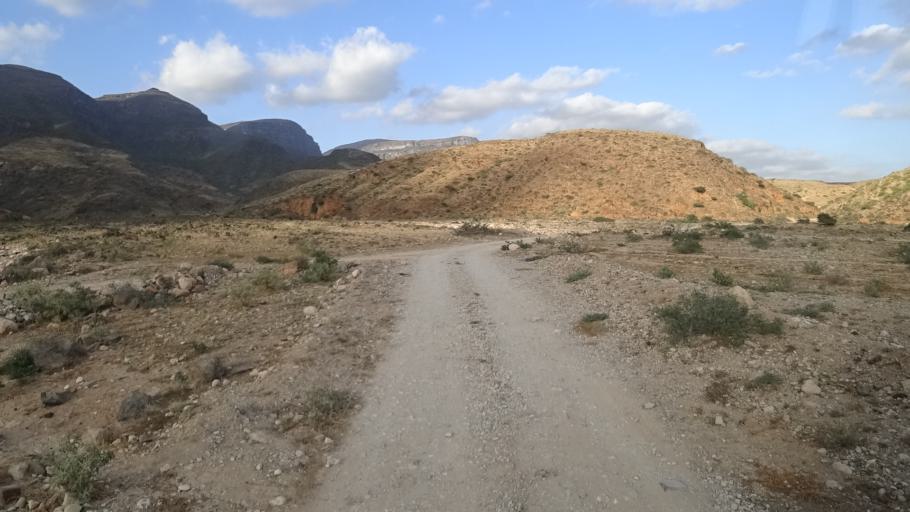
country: OM
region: Zufar
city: Salalah
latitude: 16.9915
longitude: 53.8469
